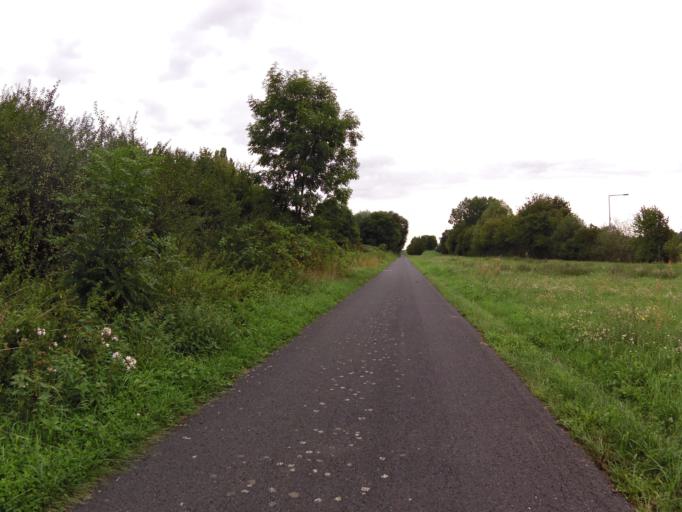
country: DE
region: Bavaria
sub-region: Regierungsbezirk Unterfranken
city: Gadheim
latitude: 50.0181
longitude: 10.3711
